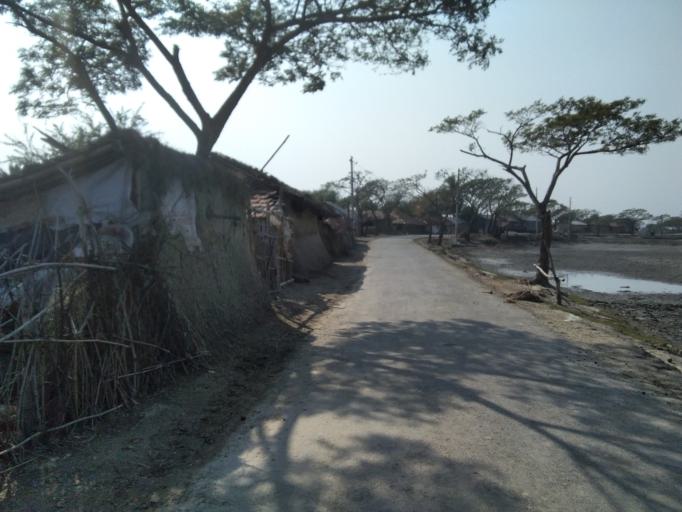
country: IN
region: West Bengal
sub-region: North 24 Parganas
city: Taki
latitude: 22.6343
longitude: 89.0126
